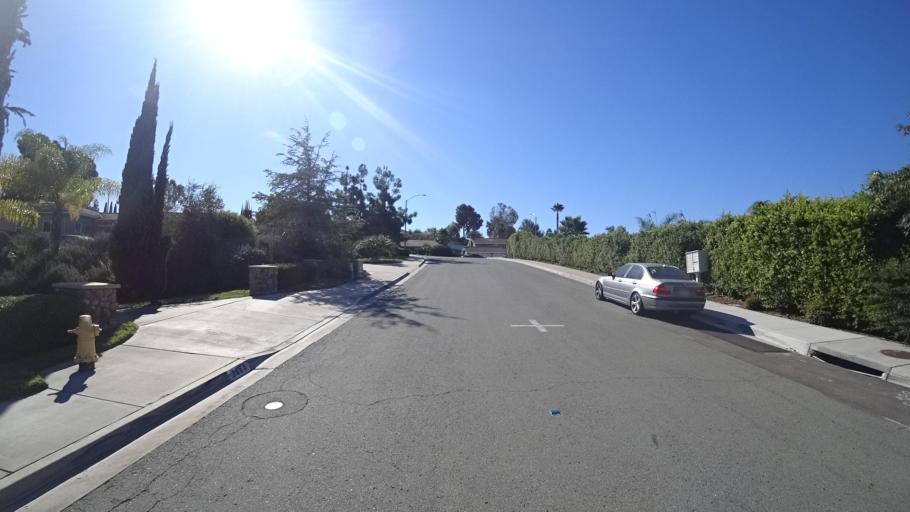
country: US
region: California
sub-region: San Diego County
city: Bonita
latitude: 32.6728
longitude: -117.0106
